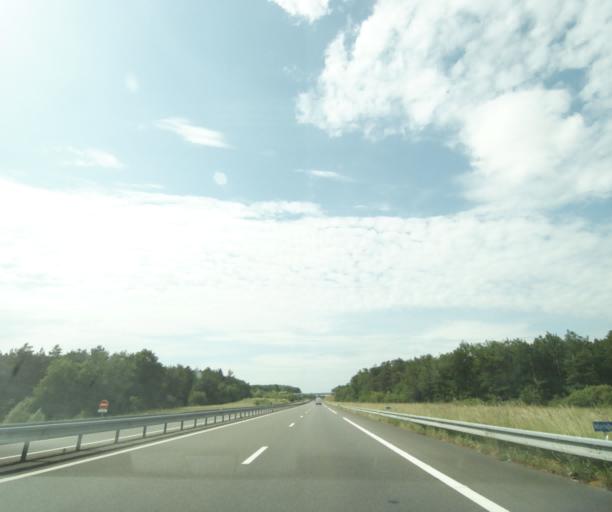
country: FR
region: Pays de la Loire
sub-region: Departement de Maine-et-Loire
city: Baune
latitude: 47.4981
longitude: -0.2793
